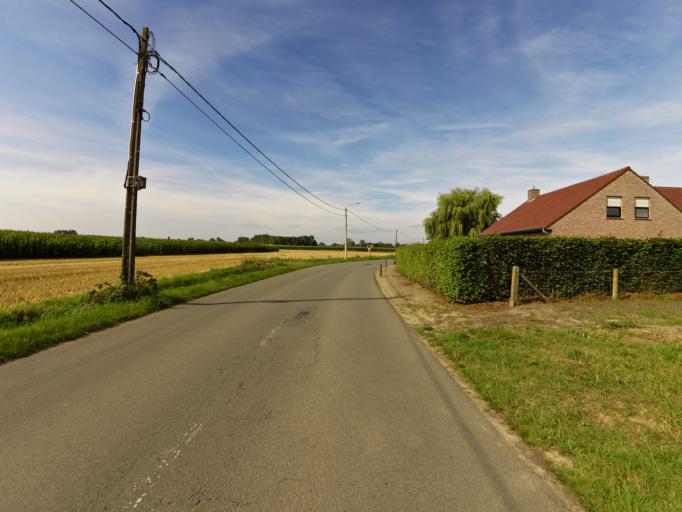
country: BE
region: Flanders
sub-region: Provincie West-Vlaanderen
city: Koekelare
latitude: 51.0463
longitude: 2.9836
